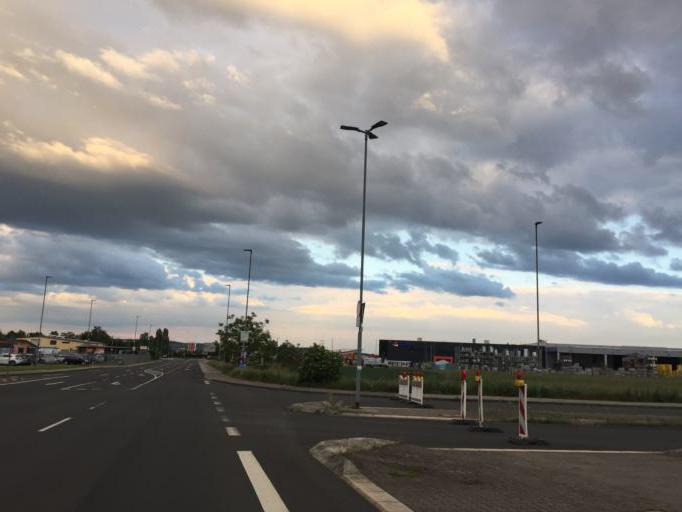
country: DE
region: Hesse
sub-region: Regierungsbezirk Darmstadt
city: Butzbach
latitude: 50.4303
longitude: 8.6805
